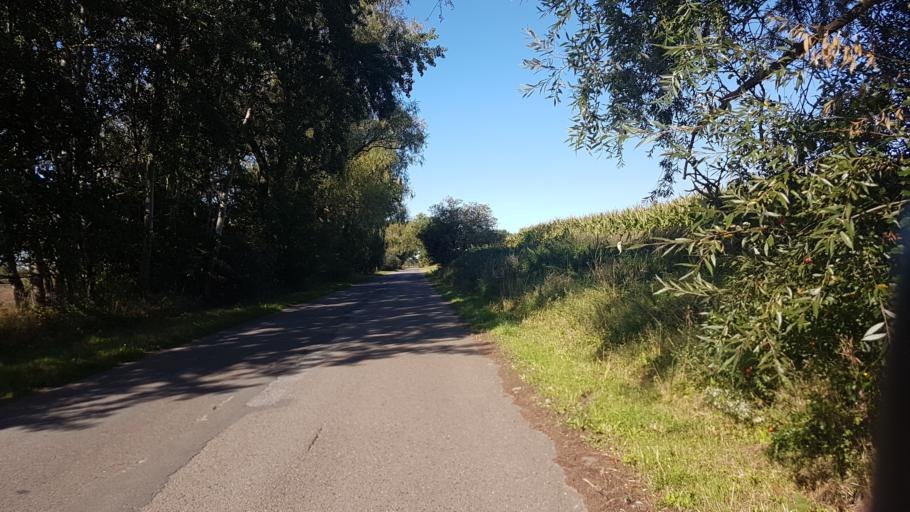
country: DE
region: Mecklenburg-Vorpommern
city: Sagard
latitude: 54.5205
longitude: 13.5248
